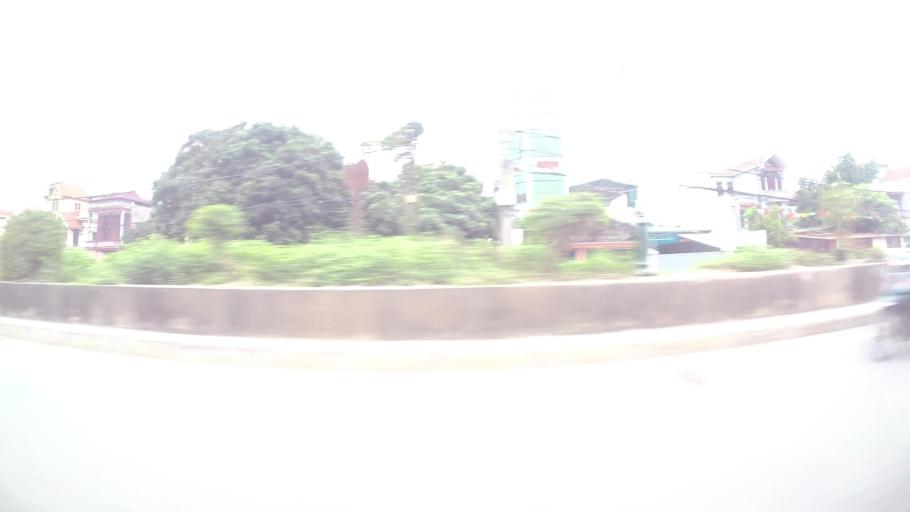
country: VN
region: Ha Noi
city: Hoan Kiem
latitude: 21.0704
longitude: 105.8813
